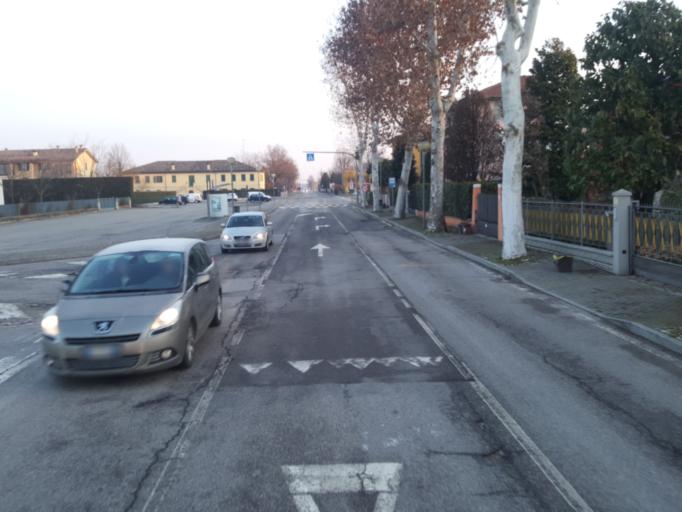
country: IT
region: Emilia-Romagna
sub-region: Provincia di Parma
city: Sorbolo
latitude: 44.8527
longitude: 10.4513
